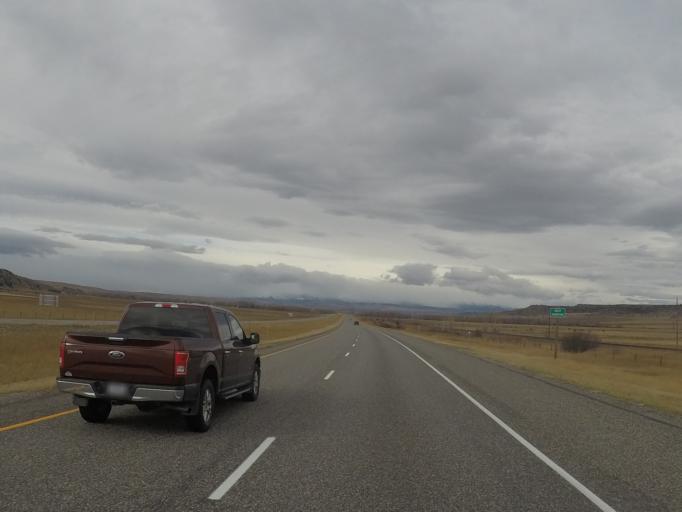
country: US
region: Montana
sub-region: Sweet Grass County
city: Big Timber
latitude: 45.7803
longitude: -109.8056
